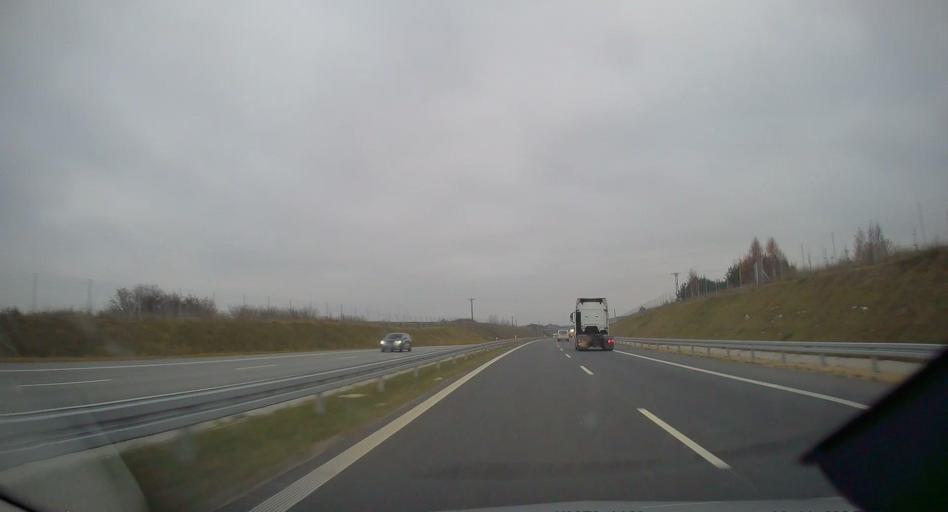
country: PL
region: Silesian Voivodeship
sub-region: Powiat bedzinski
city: Mierzecice
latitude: 50.4419
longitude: 19.1445
